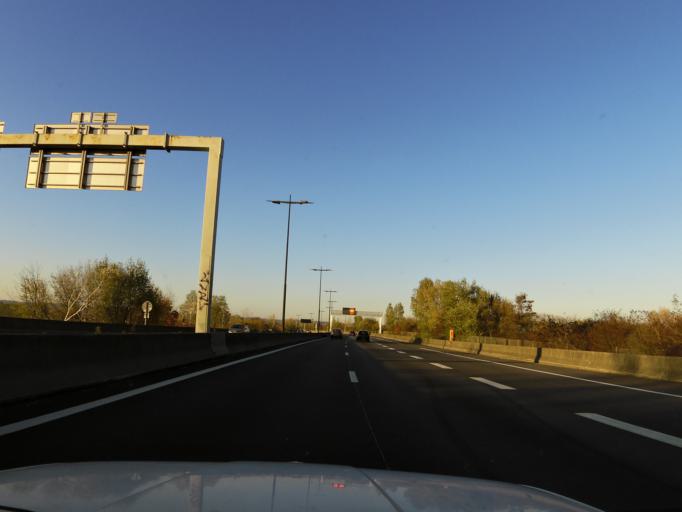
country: FR
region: Rhone-Alpes
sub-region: Departement du Rhone
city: Decines-Charpieu
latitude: 45.7864
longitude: 4.9560
